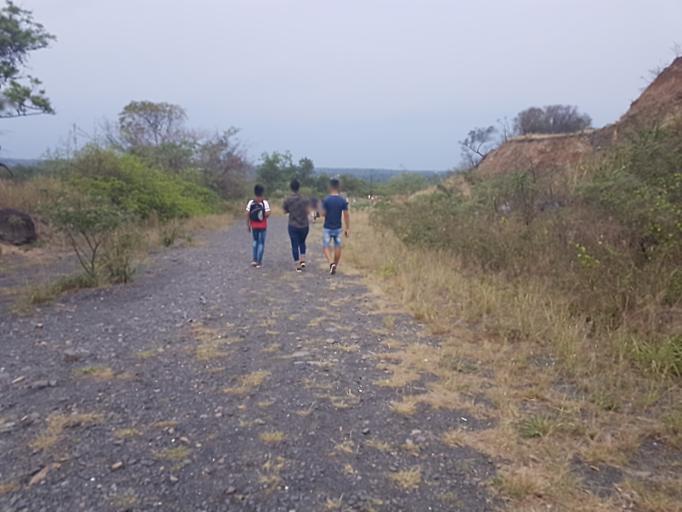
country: PY
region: Central
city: Nemby
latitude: -25.4046
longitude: -57.5366
